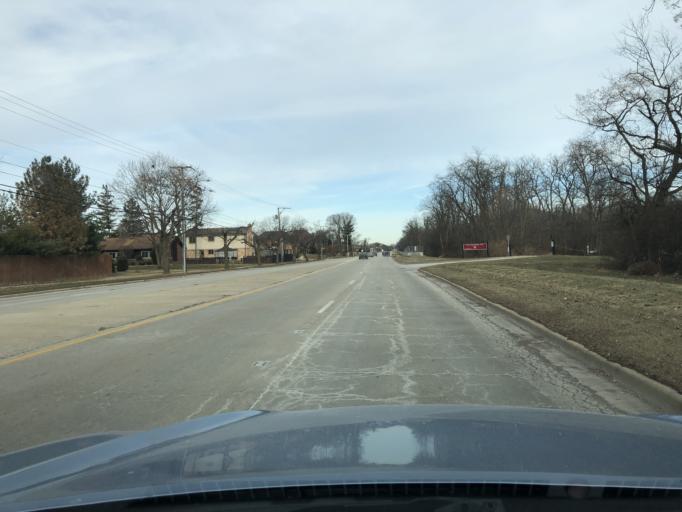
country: US
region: Illinois
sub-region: Cook County
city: Prospect Heights
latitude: 42.0886
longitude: -87.8917
